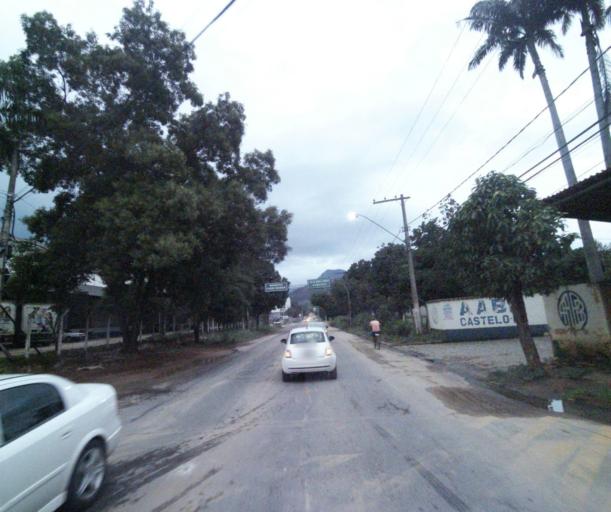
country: BR
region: Espirito Santo
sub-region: Castelo
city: Castelo
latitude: -20.6319
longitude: -41.2049
